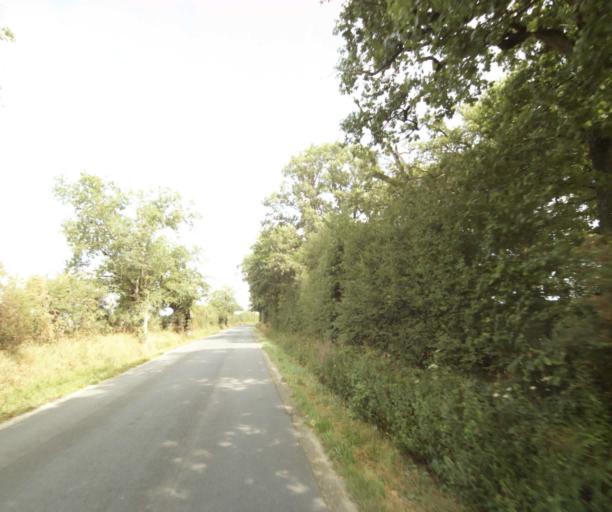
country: FR
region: Pays de la Loire
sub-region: Departement de la Sarthe
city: Sable-sur-Sarthe
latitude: 47.8120
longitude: -0.3150
